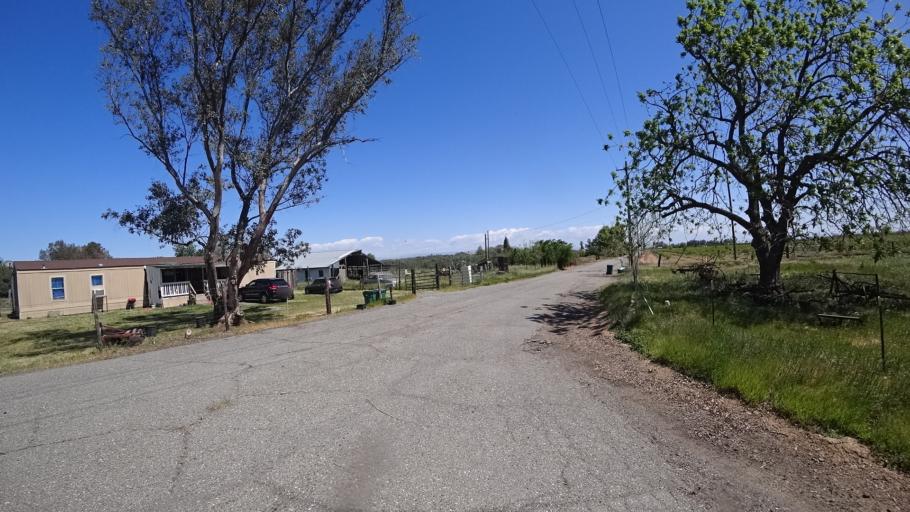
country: US
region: California
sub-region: Glenn County
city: Orland
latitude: 39.7892
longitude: -122.2028
